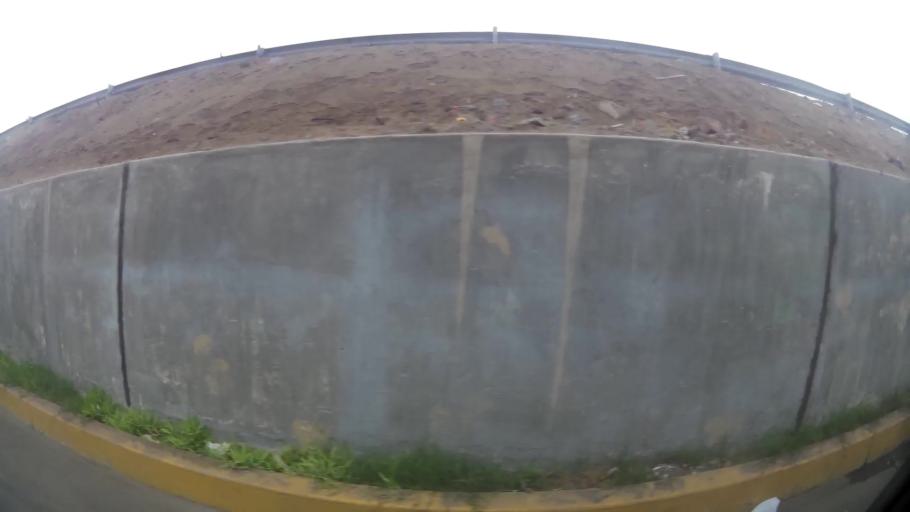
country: PE
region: Lima
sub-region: Provincia de Huaral
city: Chancay
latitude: -11.5950
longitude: -77.2558
